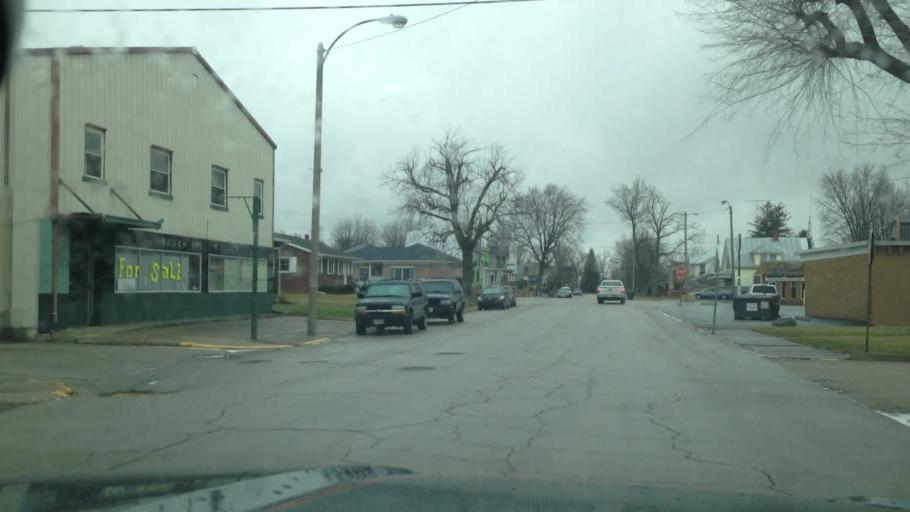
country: US
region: Ohio
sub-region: Darke County
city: Union City
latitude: 40.1995
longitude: -84.8066
